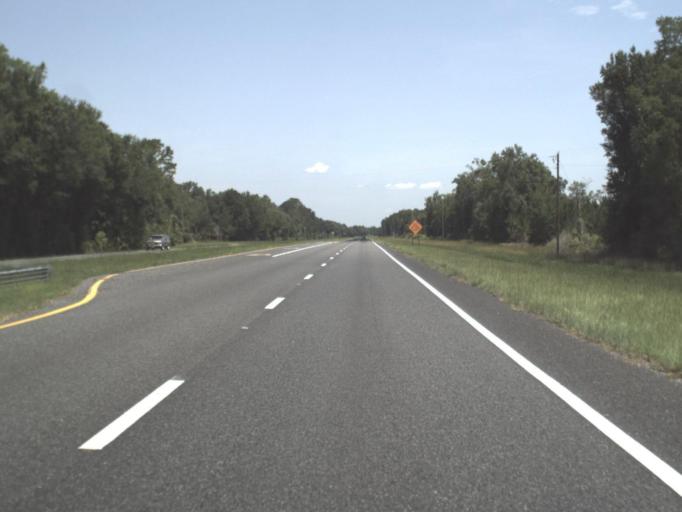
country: US
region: Florida
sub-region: Taylor County
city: Steinhatchee
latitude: 29.7364
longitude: -83.3163
